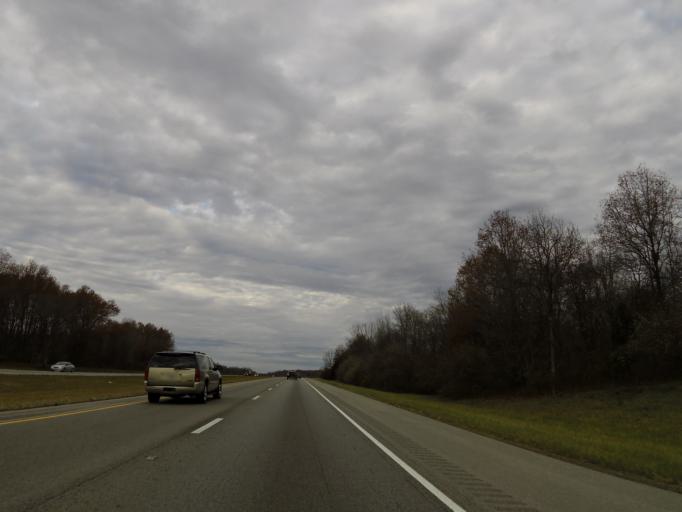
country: US
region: Illinois
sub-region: Clinton County
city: Wamac
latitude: 38.3723
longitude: -89.0974
